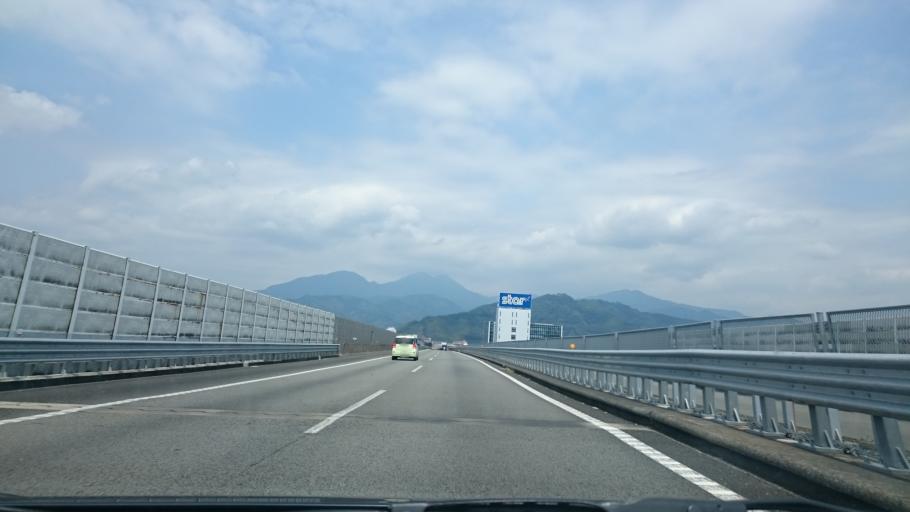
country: JP
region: Shizuoka
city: Shizuoka-shi
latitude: 34.9939
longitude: 138.4352
